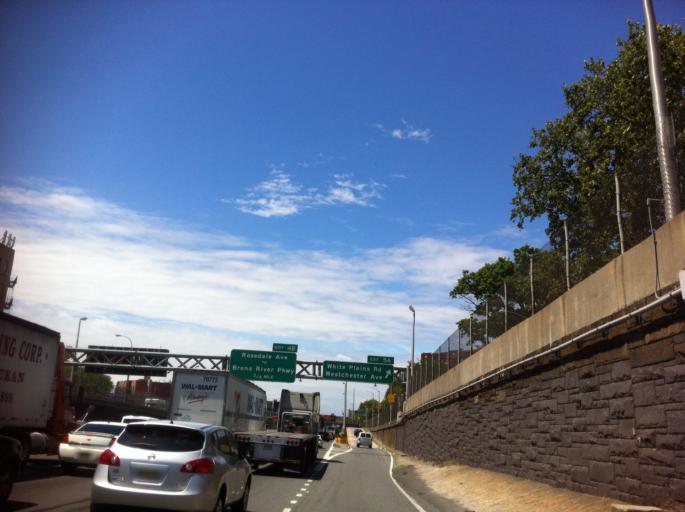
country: US
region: New York
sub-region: Bronx
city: The Bronx
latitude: 40.8308
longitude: -73.8519
